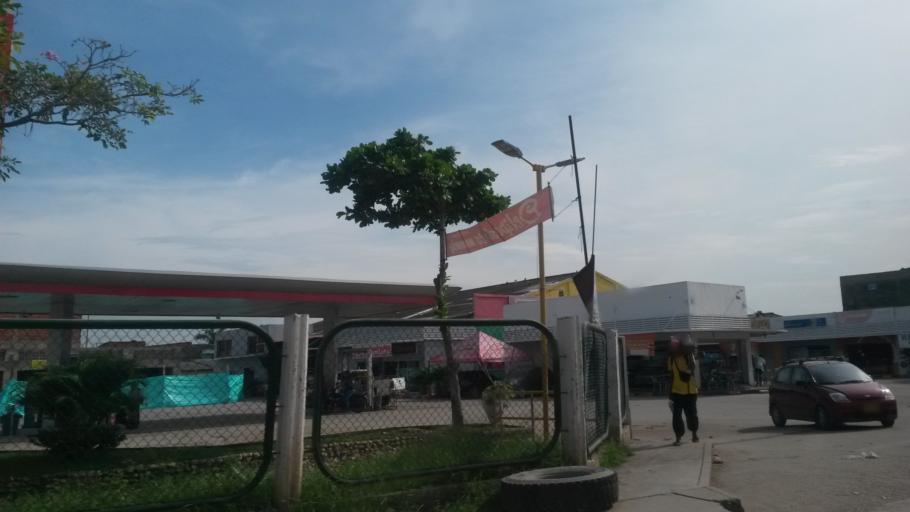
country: CO
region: Bolivar
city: Cartagena
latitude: 10.4021
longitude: -75.4735
